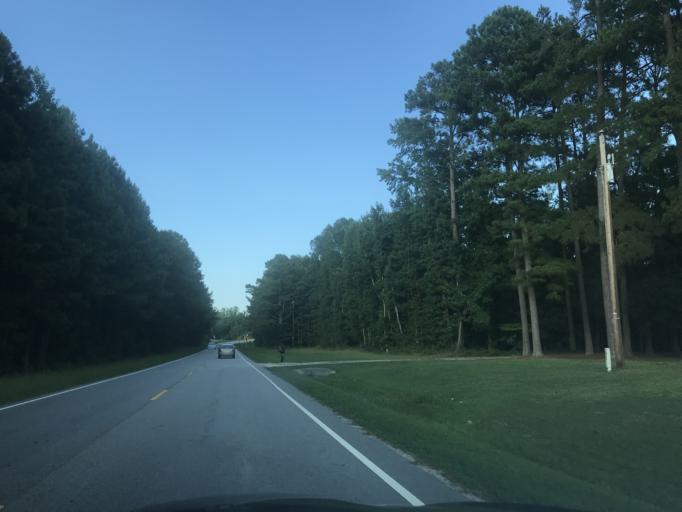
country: US
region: North Carolina
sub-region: Wake County
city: Rolesville
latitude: 35.9366
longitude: -78.4327
